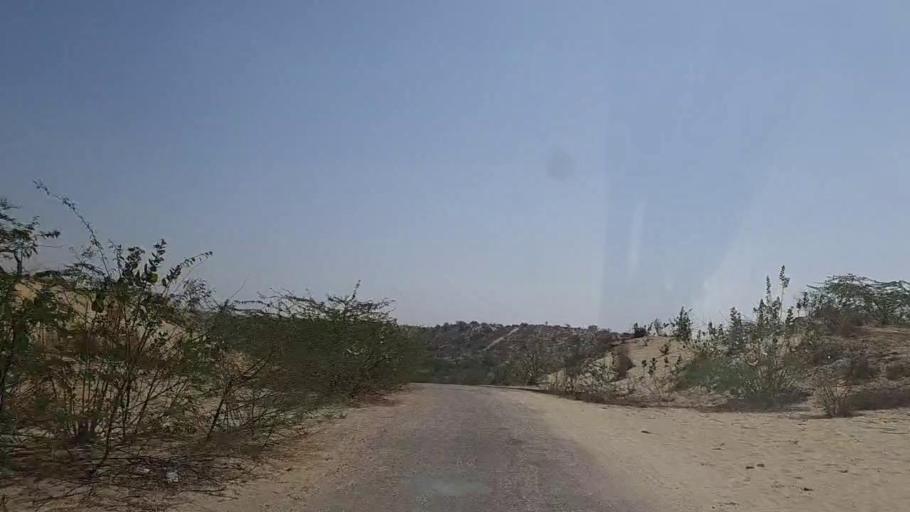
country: PK
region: Sindh
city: Diplo
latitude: 24.5174
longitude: 69.3625
